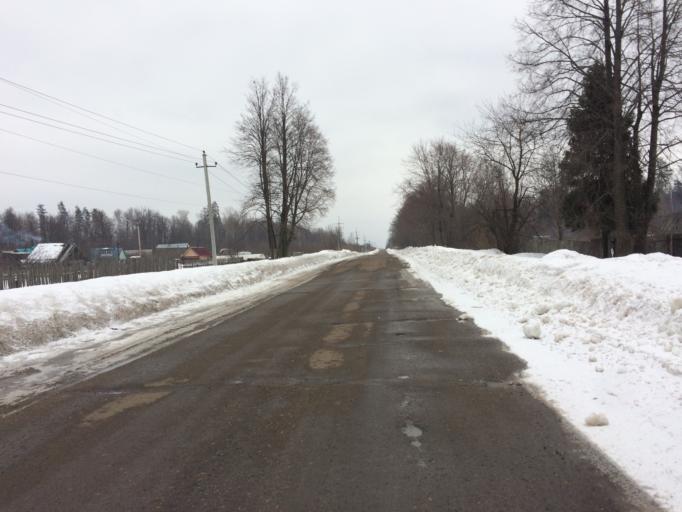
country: RU
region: Mariy-El
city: Mochalishche
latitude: 56.5457
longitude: 48.4095
